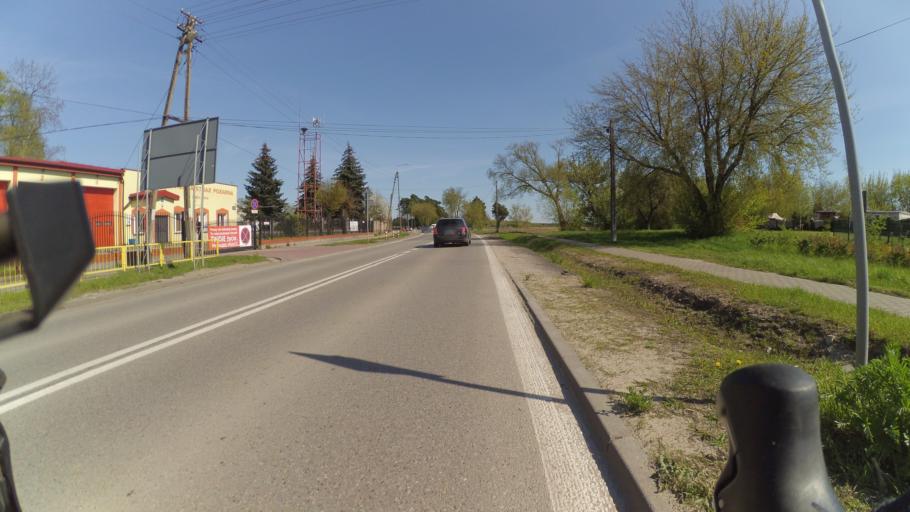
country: PL
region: Masovian Voivodeship
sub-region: Powiat warszawski zachodni
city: Jozefow
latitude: 52.2618
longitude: 20.6785
